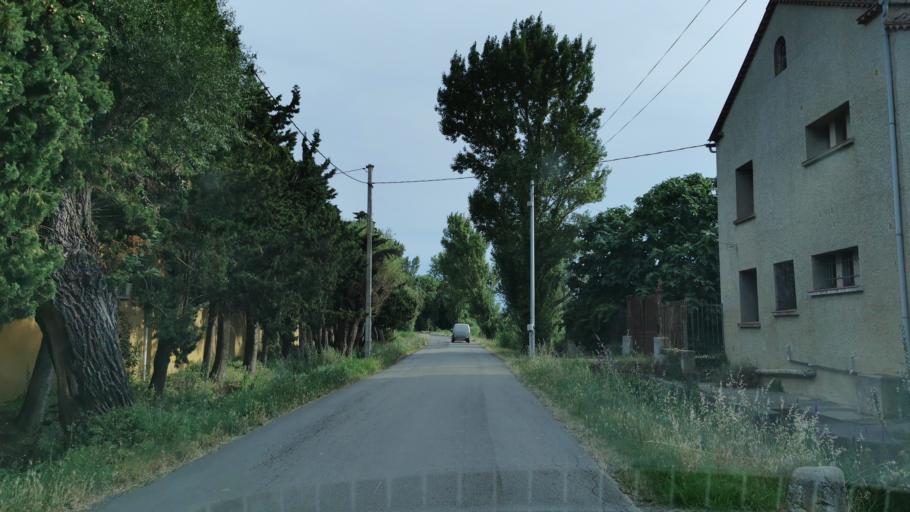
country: FR
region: Languedoc-Roussillon
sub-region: Departement de l'Aude
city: Narbonne
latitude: 43.1997
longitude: 2.9967
